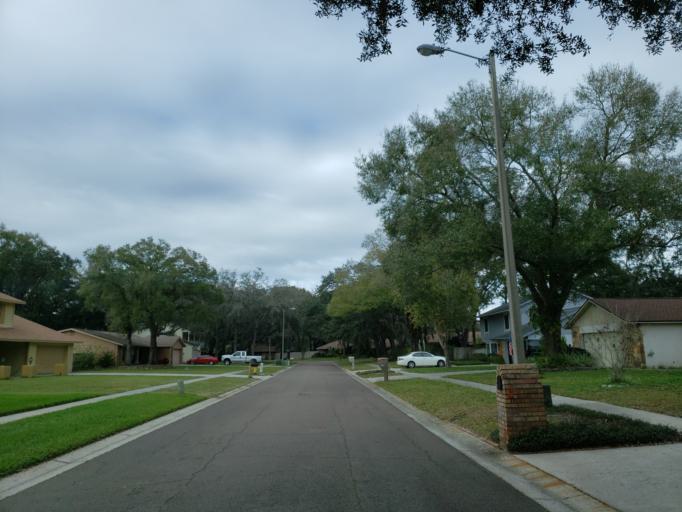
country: US
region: Florida
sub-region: Hillsborough County
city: Bloomingdale
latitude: 27.8821
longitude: -82.2821
